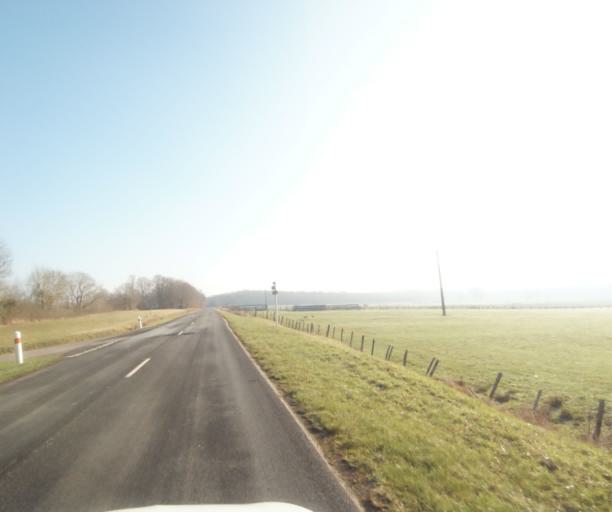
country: FR
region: Champagne-Ardenne
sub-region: Departement de la Haute-Marne
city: Laneuville-a-Remy
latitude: 48.4929
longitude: 4.8729
